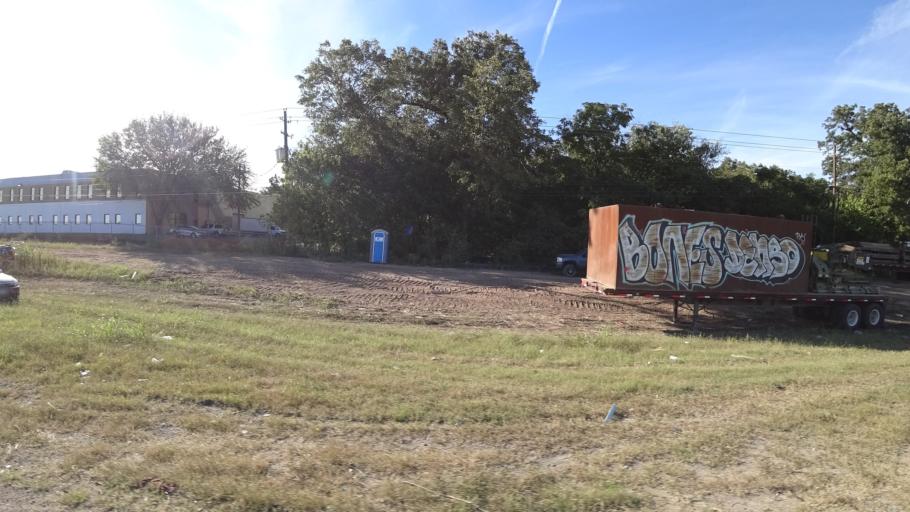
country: US
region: Texas
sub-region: Travis County
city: Austin
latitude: 30.2602
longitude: -97.6750
